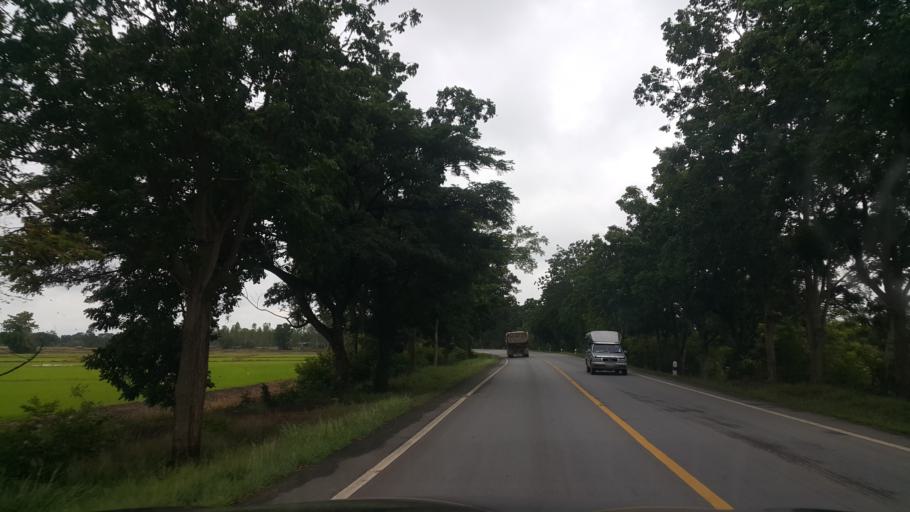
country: TH
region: Sukhothai
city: Sawankhalok
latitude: 17.3395
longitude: 99.7425
